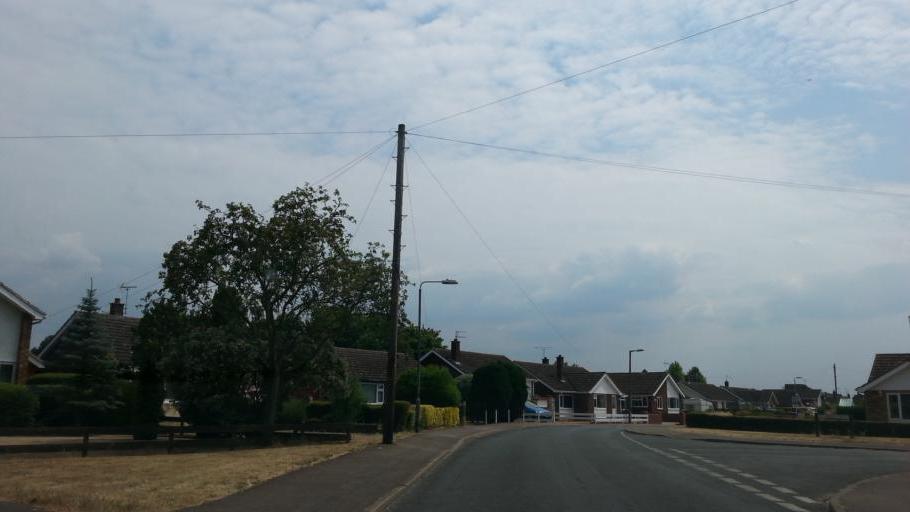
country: GB
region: England
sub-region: Suffolk
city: Lakenheath
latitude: 52.4163
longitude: 0.5289
